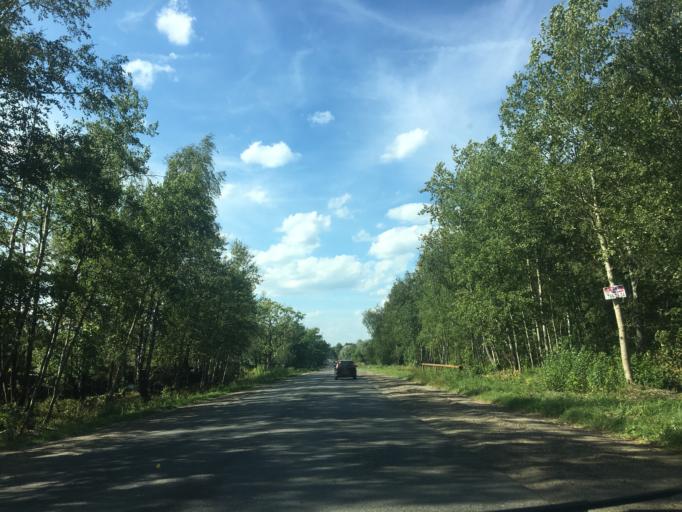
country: RU
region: Moskovskaya
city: Vidnoye
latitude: 55.5264
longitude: 37.6757
